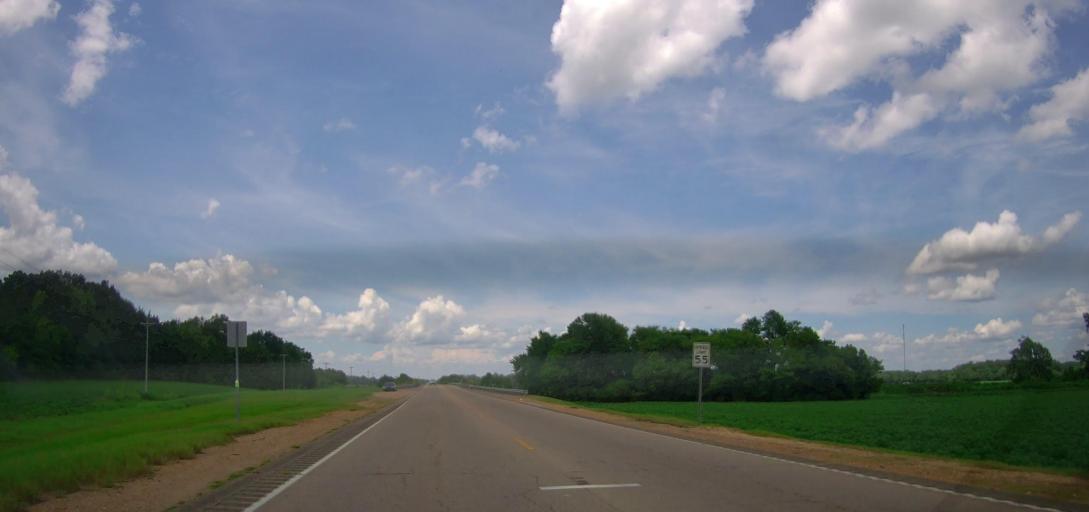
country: US
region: Mississippi
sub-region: Lee County
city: Shannon
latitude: 34.1356
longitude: -88.7194
